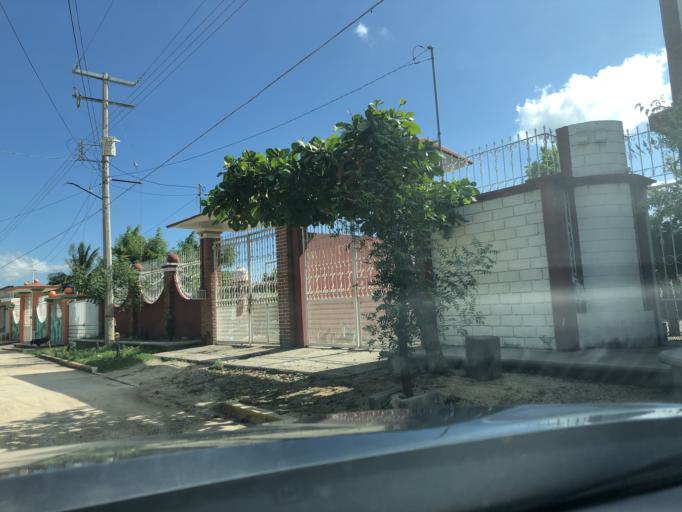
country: MX
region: Oaxaca
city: San Jeronimo Ixtepec
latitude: 16.5548
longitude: -95.1061
